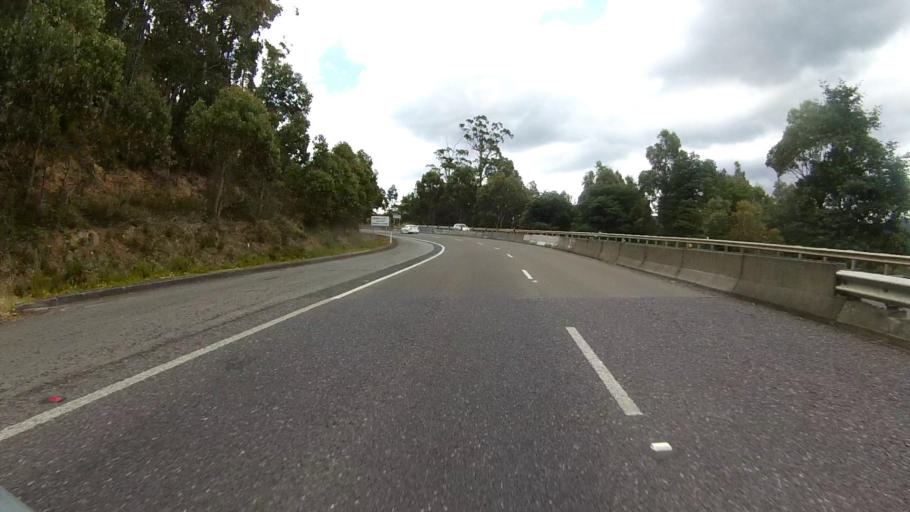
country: AU
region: Tasmania
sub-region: Kingborough
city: Margate
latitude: -42.9821
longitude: 147.1781
